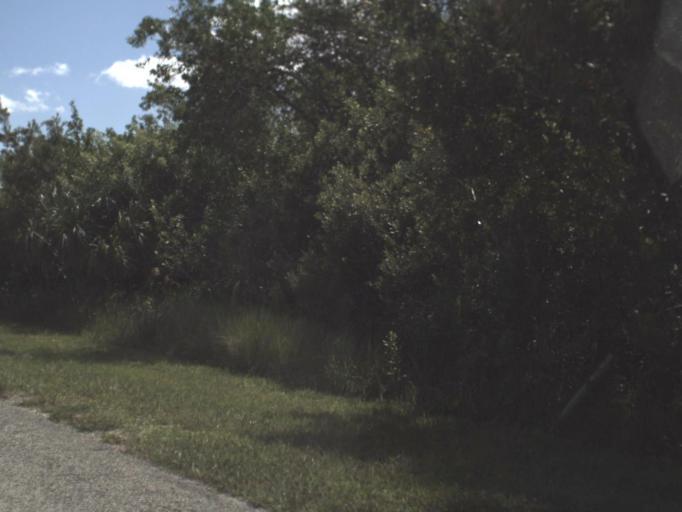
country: US
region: Florida
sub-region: Collier County
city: Marco
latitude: 25.9590
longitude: -81.4921
